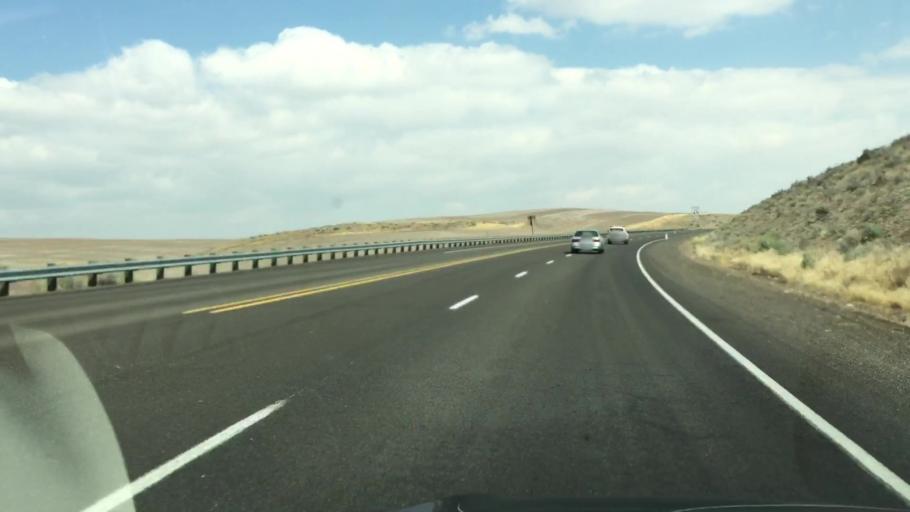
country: US
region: Oregon
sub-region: Wasco County
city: The Dalles
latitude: 45.4612
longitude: -121.1243
